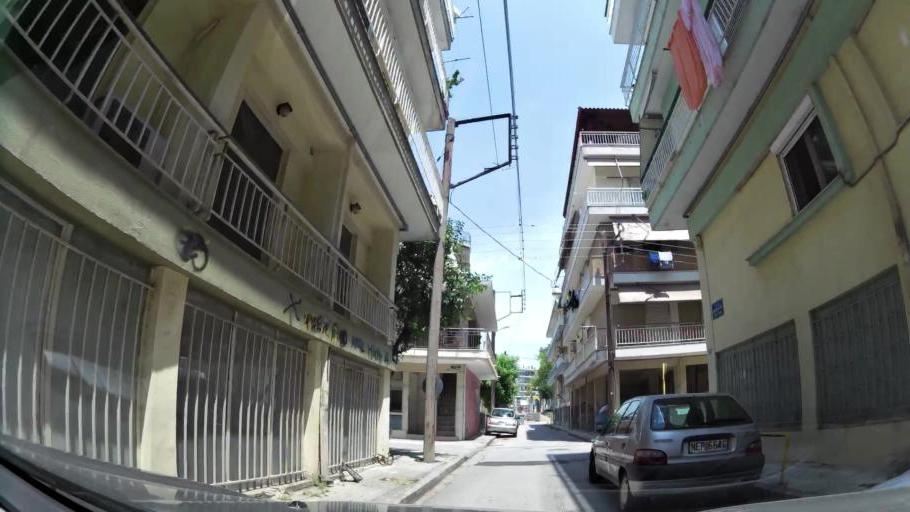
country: GR
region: Central Macedonia
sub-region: Nomos Thessalonikis
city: Evosmos
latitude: 40.6593
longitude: 22.9097
